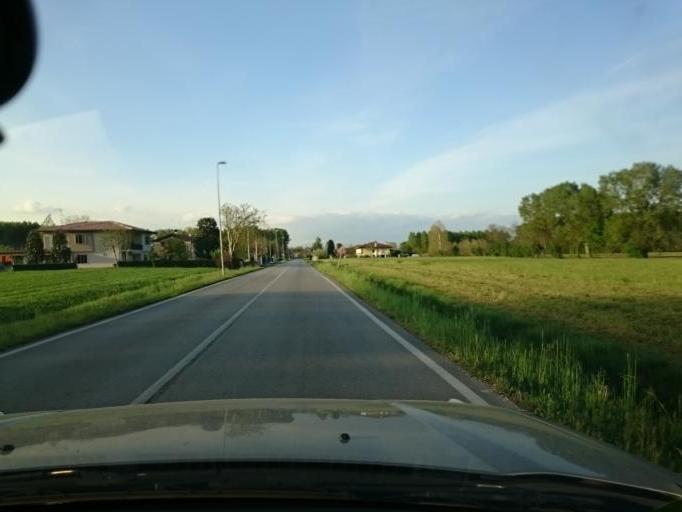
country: IT
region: Veneto
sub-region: Provincia di Treviso
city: Badoere
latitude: 45.6414
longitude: 12.1043
